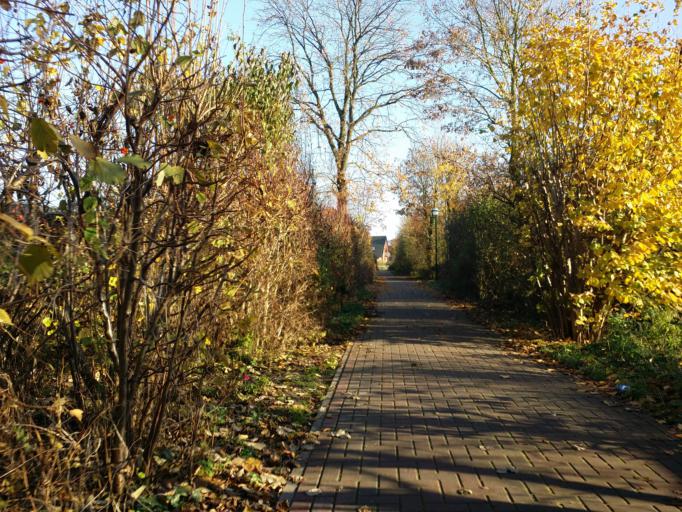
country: DE
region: Lower Saxony
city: Rotenburg
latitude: 53.0957
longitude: 9.3905
